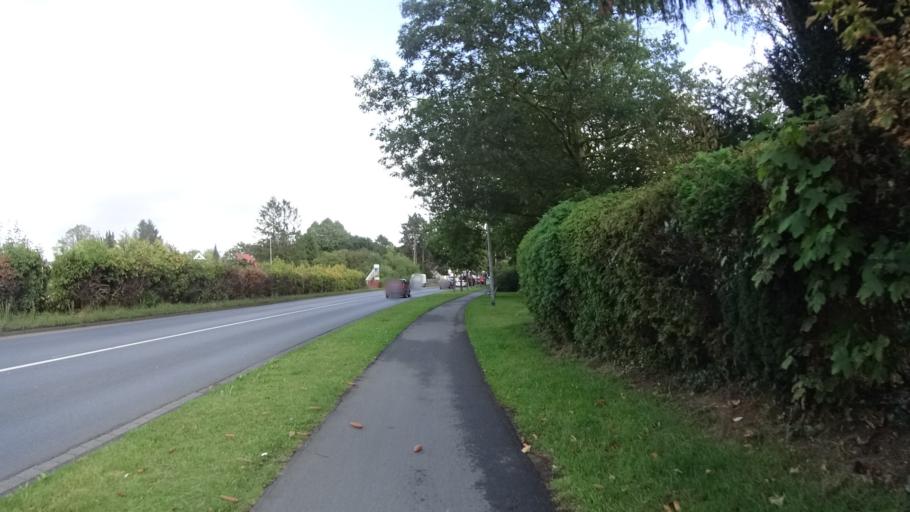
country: DE
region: Lower Saxony
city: Varel
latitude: 53.3922
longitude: 8.1457
